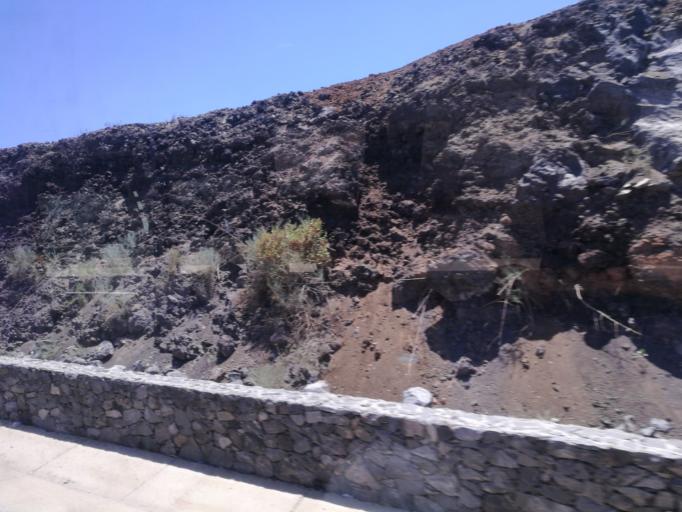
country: ES
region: Canary Islands
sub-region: Provincia de Santa Cruz de Tenerife
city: Guia de Isora
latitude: 28.1941
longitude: -16.8109
